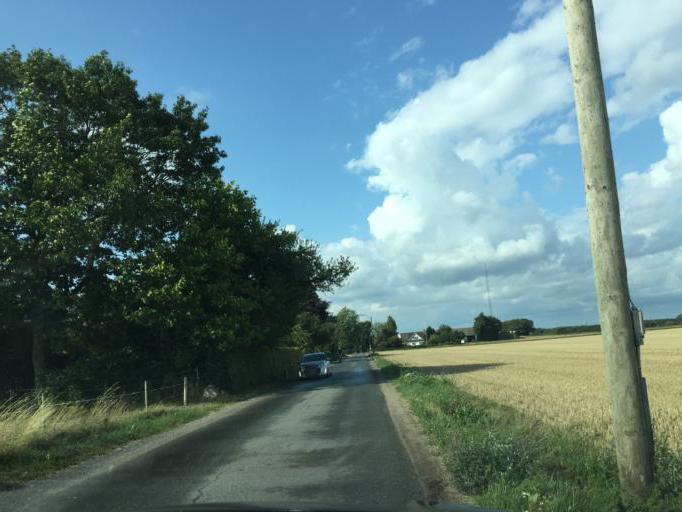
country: DK
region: South Denmark
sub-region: Odense Kommune
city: Bellinge
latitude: 55.3319
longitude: 10.3769
